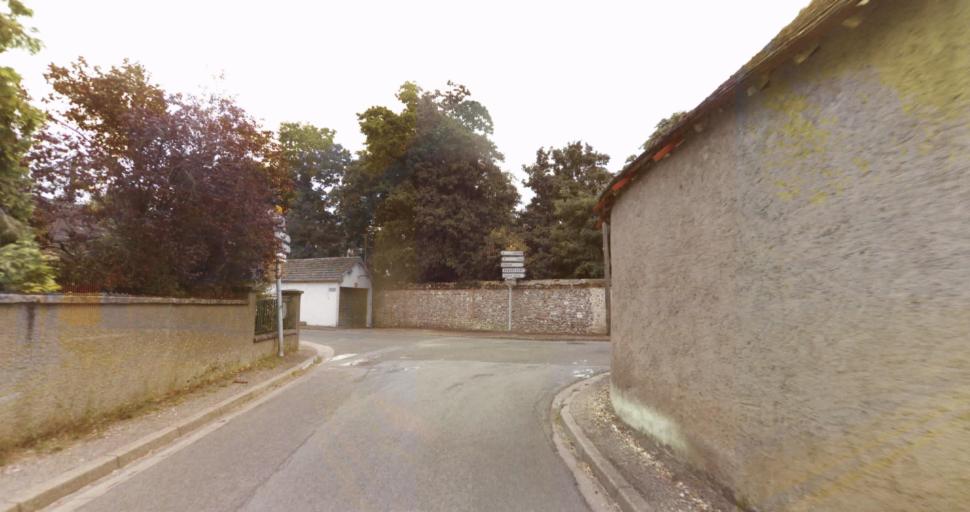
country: FR
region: Centre
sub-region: Departement d'Eure-et-Loir
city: Vert-en-Drouais
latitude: 48.7726
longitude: 1.3028
